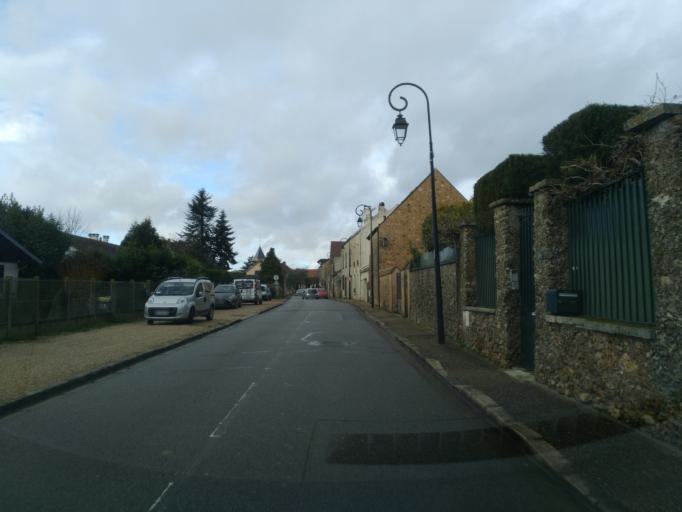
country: FR
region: Ile-de-France
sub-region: Departement des Yvelines
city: Les Alluets-le-Roi
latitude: 48.9133
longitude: 1.9212
